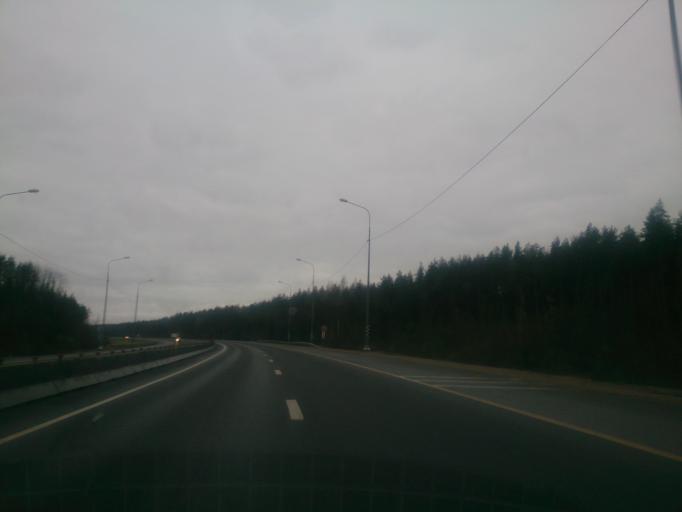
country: RU
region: Leningrad
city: Nurma
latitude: 59.4934
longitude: 30.9533
